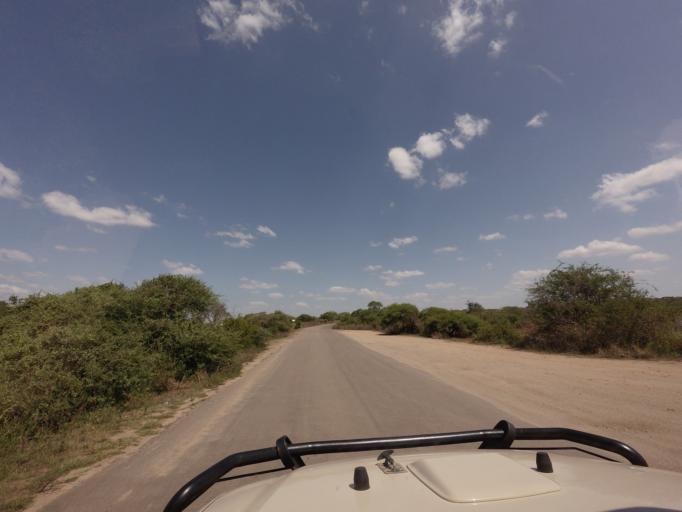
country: ZA
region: Mpumalanga
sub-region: Ehlanzeni District
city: Komatipoort
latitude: -25.1163
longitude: 31.9124
